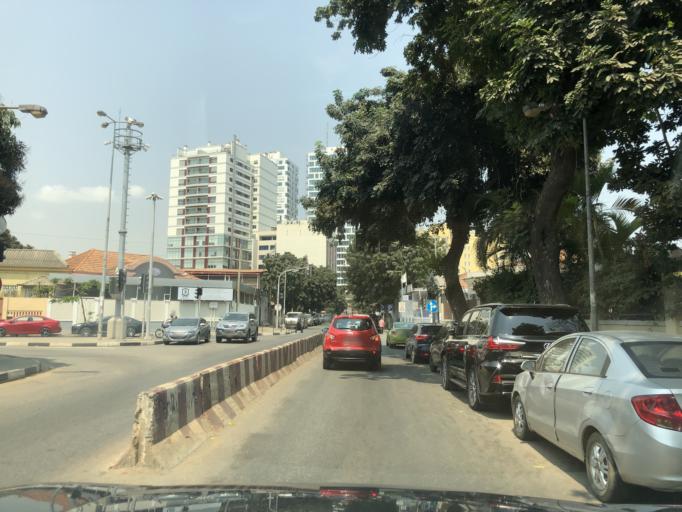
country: AO
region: Luanda
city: Luanda
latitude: -8.8180
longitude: 13.2379
